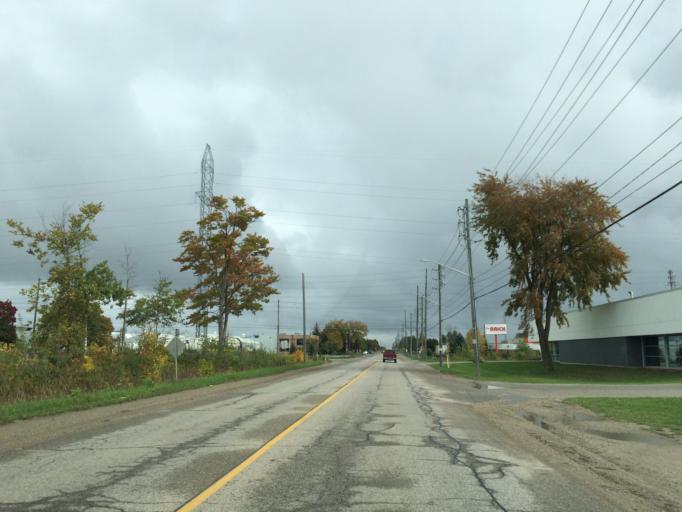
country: CA
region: Ontario
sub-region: Wellington County
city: Guelph
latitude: 43.5490
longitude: -80.2929
